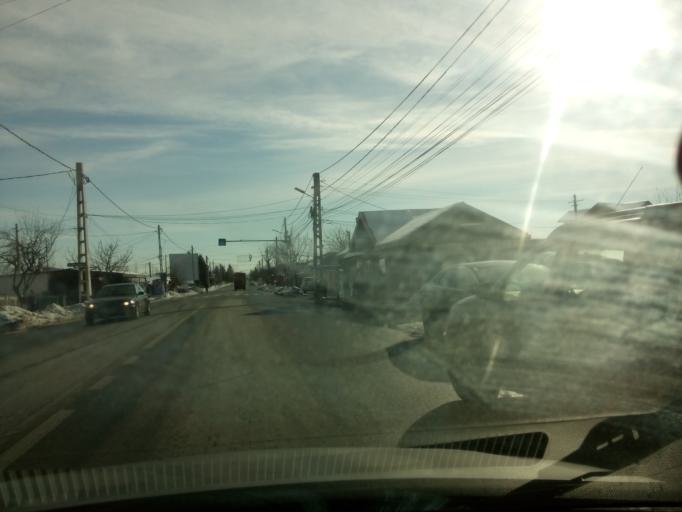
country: RO
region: Ilfov
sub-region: Comuna Popesti-Leordeni
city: Popesti-Leordeni
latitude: 44.3772
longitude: 26.1733
